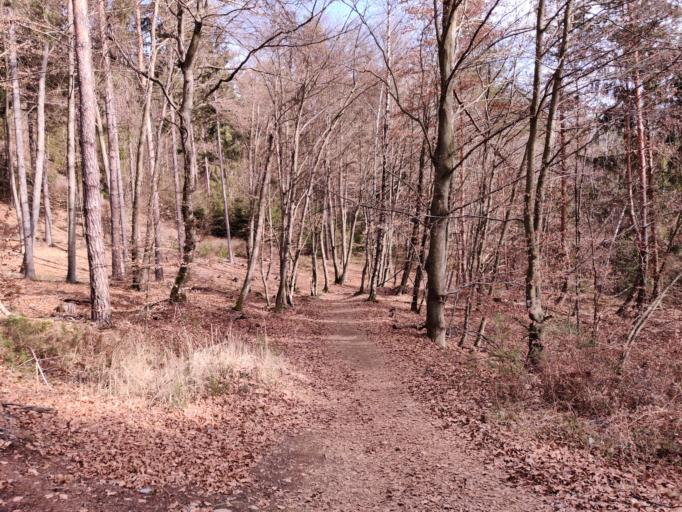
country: AT
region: Carinthia
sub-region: Klagenfurt am Woerthersee
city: Klagenfurt am Woerthersee
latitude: 46.6291
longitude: 14.2569
